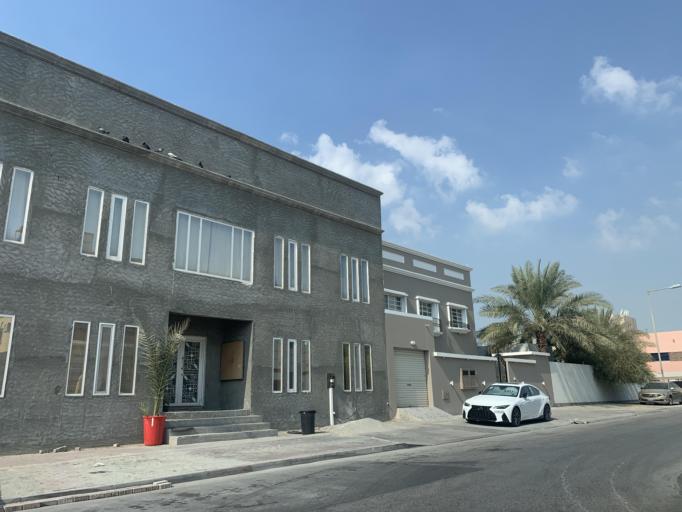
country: BH
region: Central Governorate
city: Madinat Hamad
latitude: 26.1050
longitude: 50.5005
